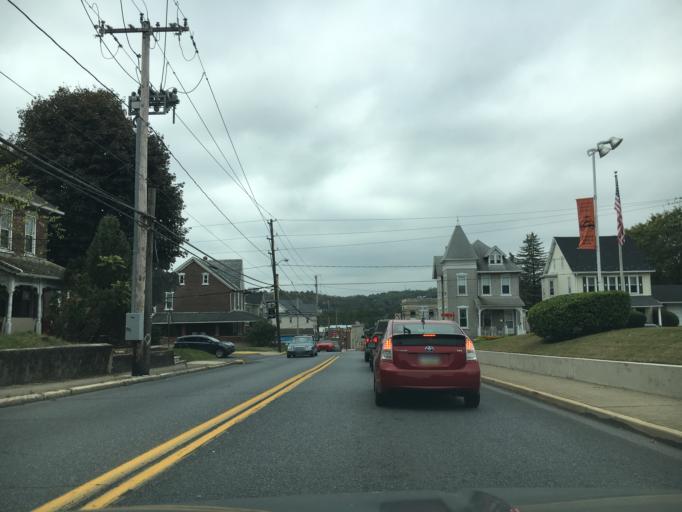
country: US
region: Pennsylvania
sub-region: Northampton County
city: Northampton
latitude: 40.6911
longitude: -75.4976
